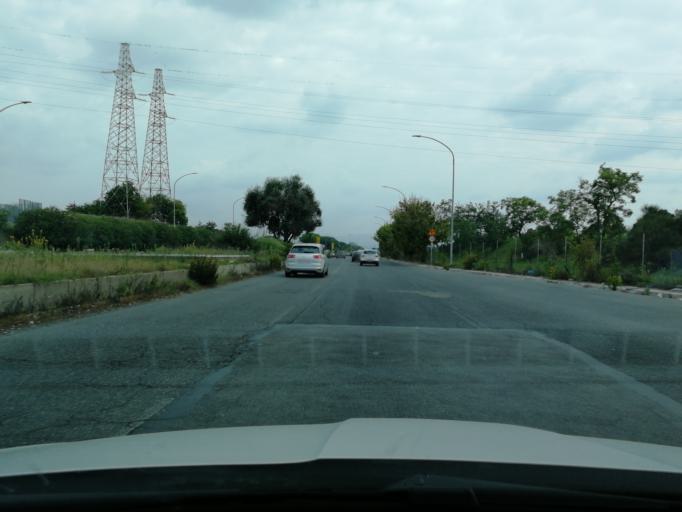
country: IT
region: Latium
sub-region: Citta metropolitana di Roma Capitale
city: Ciampino
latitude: 41.8482
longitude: 12.5759
